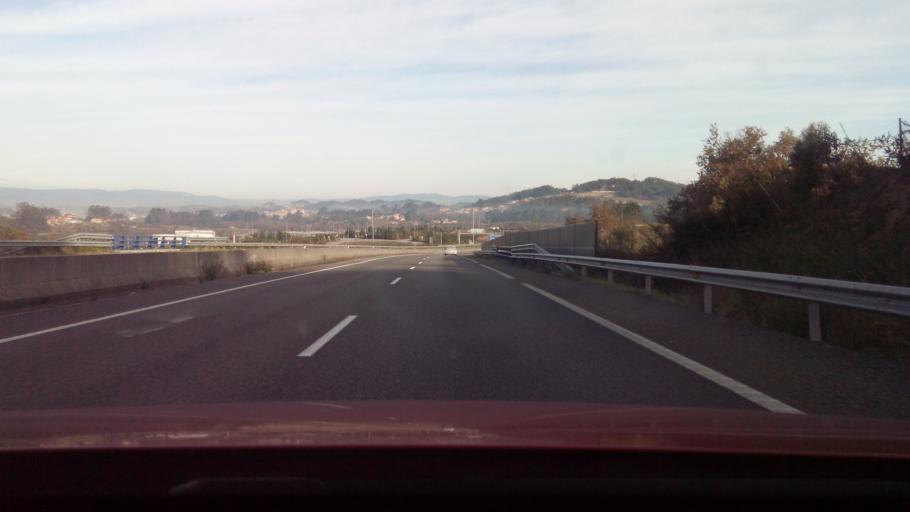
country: ES
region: Galicia
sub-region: Provincia de Pontevedra
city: Sanxenxo
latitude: 42.4234
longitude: -8.8071
